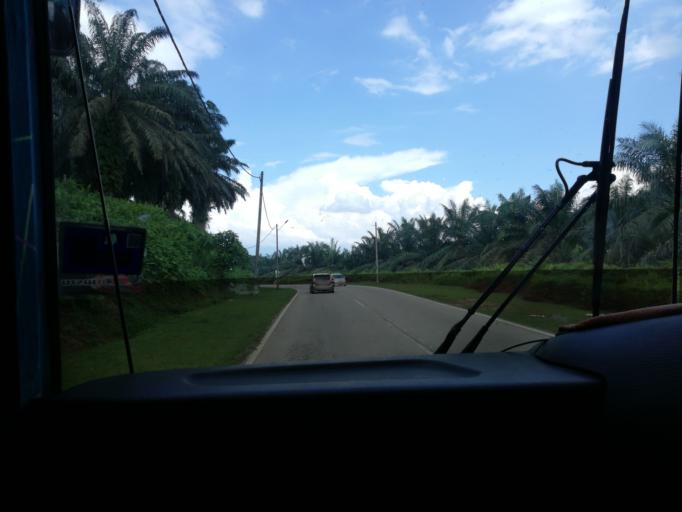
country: MY
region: Kedah
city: Kulim
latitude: 5.2675
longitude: 100.6116
